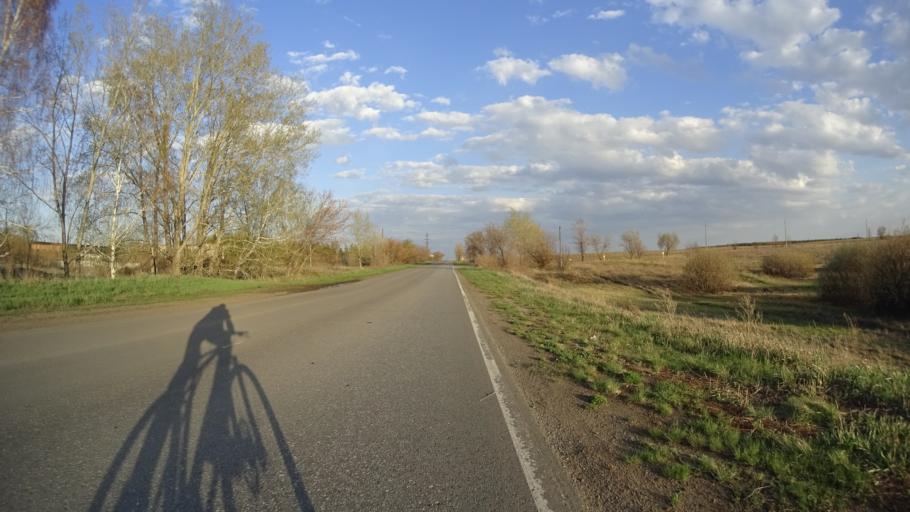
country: RU
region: Chelyabinsk
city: Troitsk
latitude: 54.0552
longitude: 61.5874
